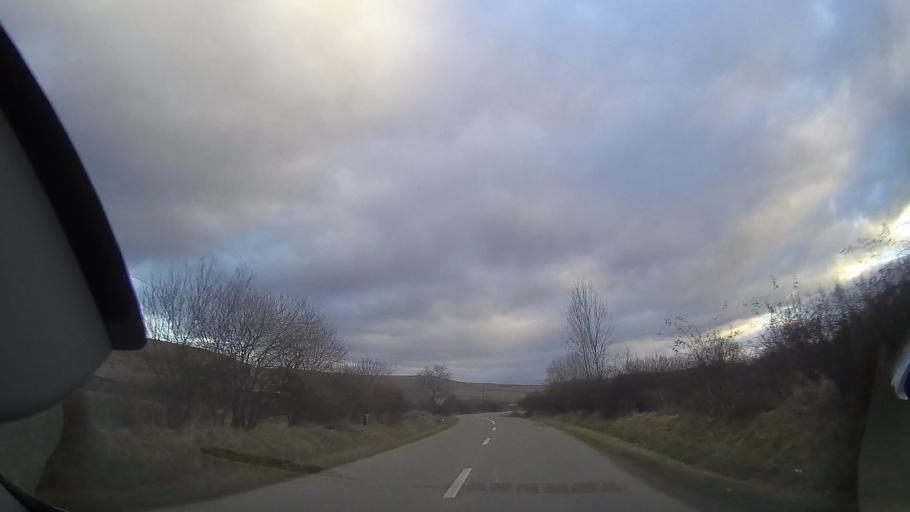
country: RO
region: Cluj
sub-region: Comuna Sancraiu
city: Sancraiu
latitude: 46.8224
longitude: 22.9931
